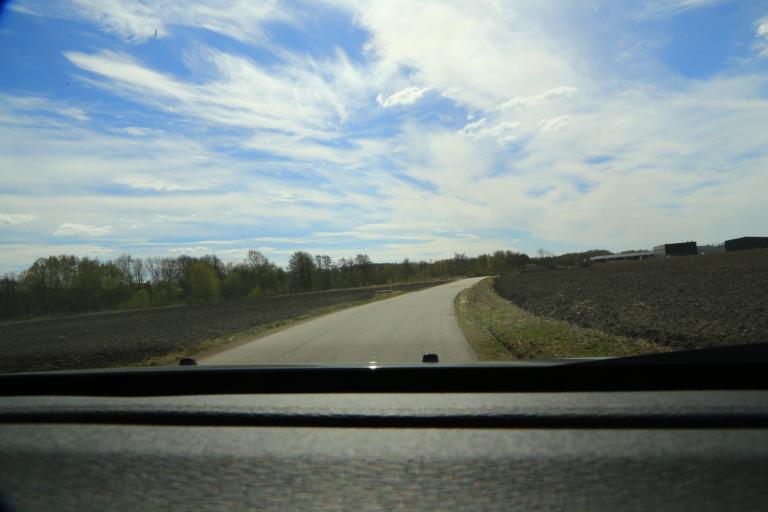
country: SE
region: Halland
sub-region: Varbergs Kommun
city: Varberg
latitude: 57.1227
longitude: 12.3094
